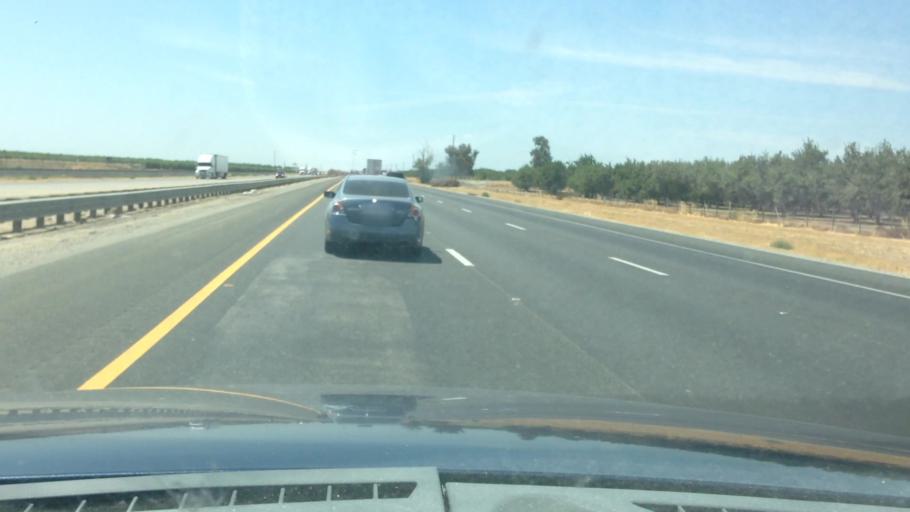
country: US
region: California
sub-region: Kern County
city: McFarland
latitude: 35.6339
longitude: -119.2169
